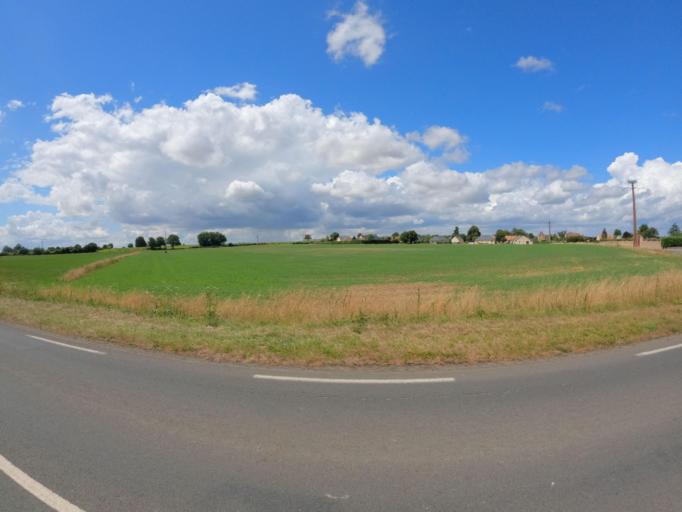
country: FR
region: Pays de la Loire
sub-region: Departement de la Sarthe
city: Brulon
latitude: 47.9514
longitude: -0.2476
